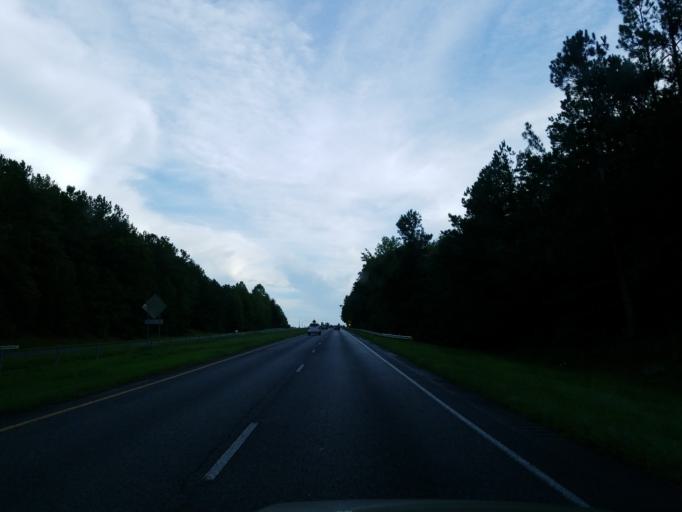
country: US
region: Georgia
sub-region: Dawson County
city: Dawsonville
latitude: 34.3842
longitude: -84.0237
